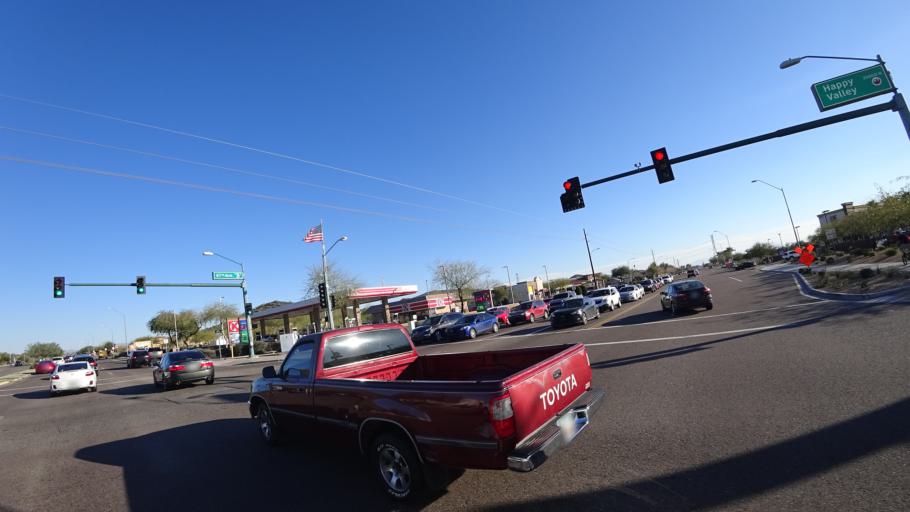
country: US
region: Arizona
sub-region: Maricopa County
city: Sun City
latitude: 33.7121
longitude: -112.2033
